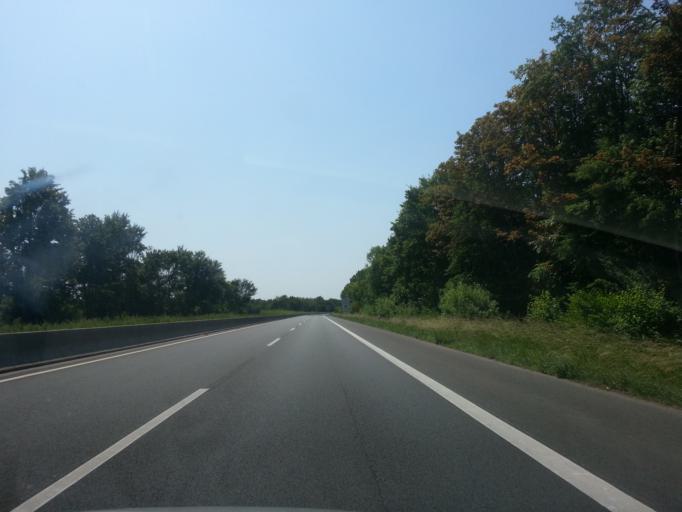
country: DE
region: Hesse
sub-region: Regierungsbezirk Darmstadt
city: Gross-Zimmern
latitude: 49.8792
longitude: 8.8057
